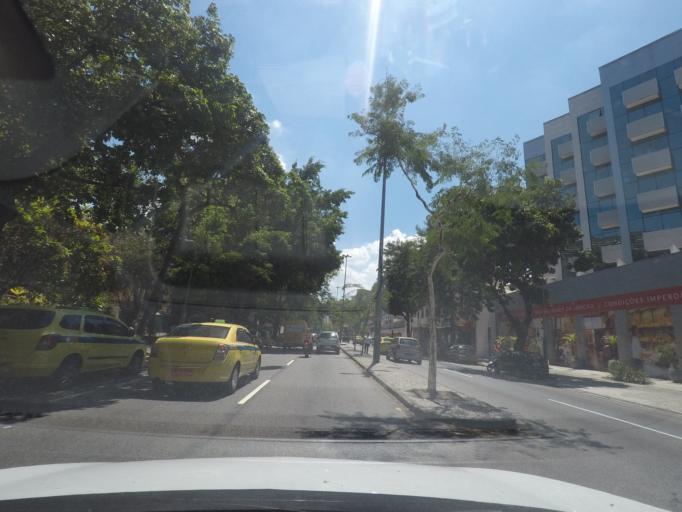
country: BR
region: Rio de Janeiro
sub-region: Rio De Janeiro
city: Rio de Janeiro
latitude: -22.9141
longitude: -43.2373
